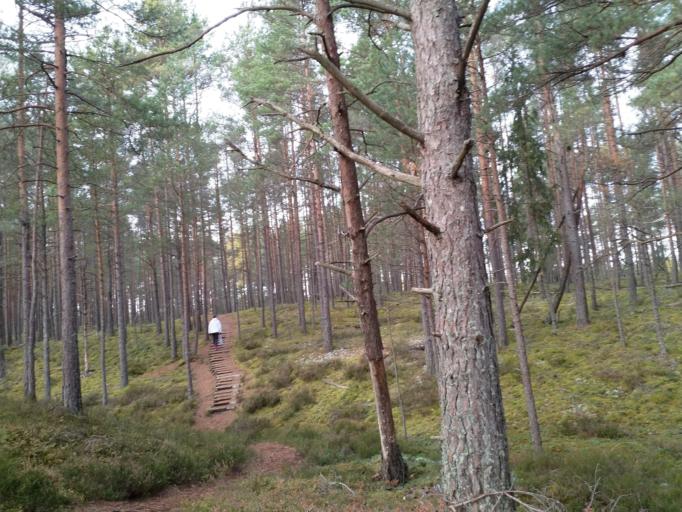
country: LV
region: Dundaga
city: Dundaga
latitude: 57.6493
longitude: 22.2567
